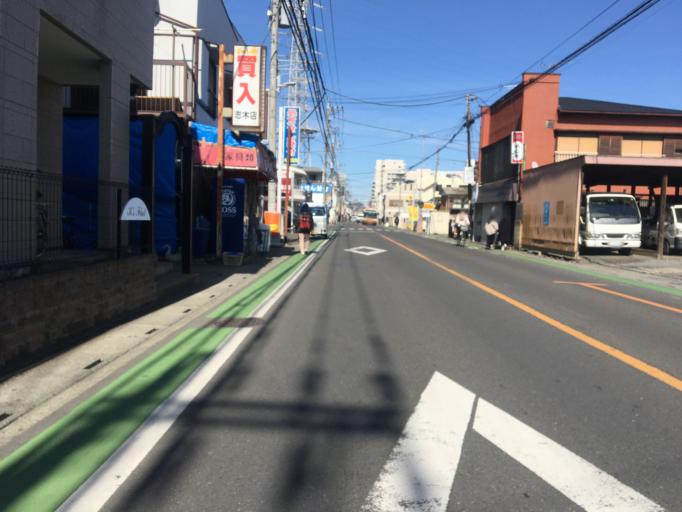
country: JP
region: Saitama
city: Shiki
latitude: 35.8192
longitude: 139.5712
